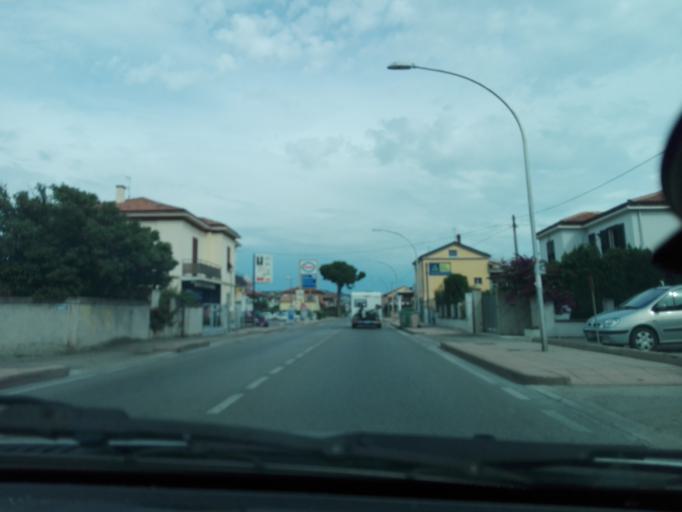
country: IT
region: Abruzzo
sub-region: Provincia di Pescara
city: San Martino Bassa
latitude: 42.5257
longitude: 14.1388
